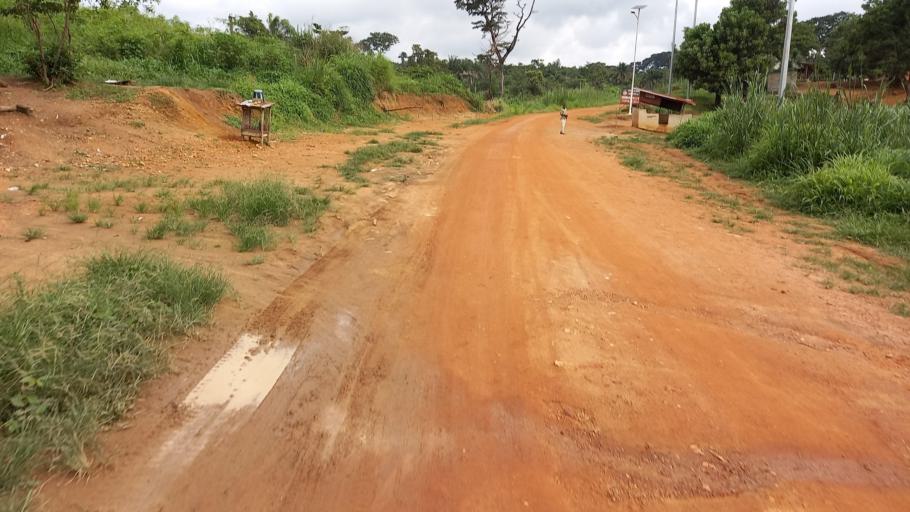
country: SL
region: Eastern Province
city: Kailahun
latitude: 8.2935
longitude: -10.5760
